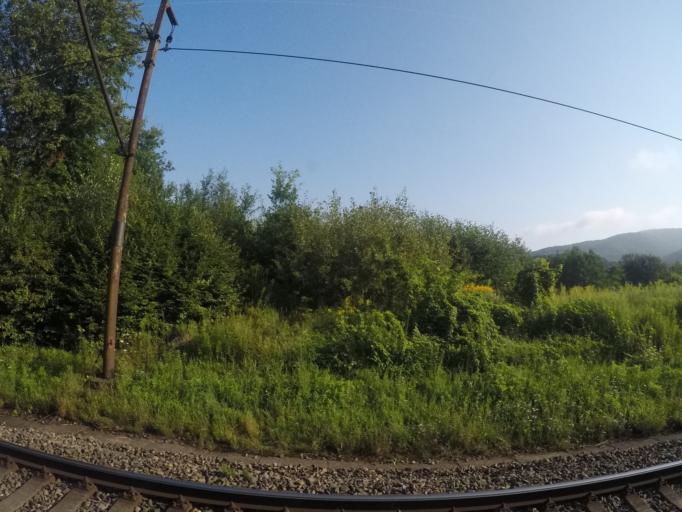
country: SK
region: Kosicky
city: Gelnica
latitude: 48.9141
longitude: 20.9494
